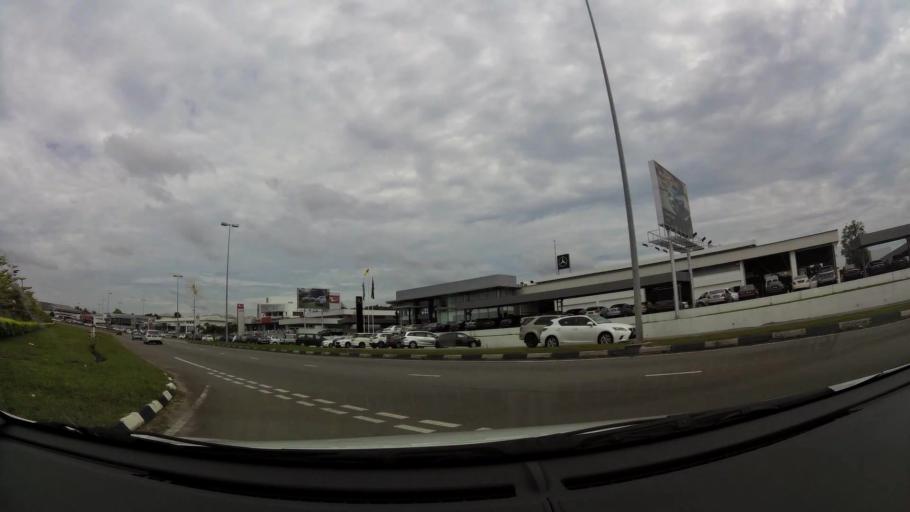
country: BN
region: Brunei and Muara
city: Bandar Seri Begawan
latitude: 4.8950
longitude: 114.9034
